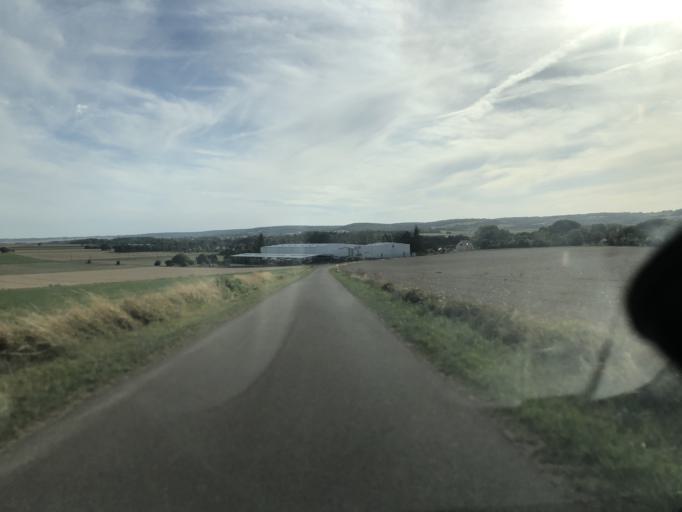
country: FR
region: Bourgogne
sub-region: Departement de l'Yonne
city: Aillant-sur-Tholon
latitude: 47.9283
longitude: 3.3735
